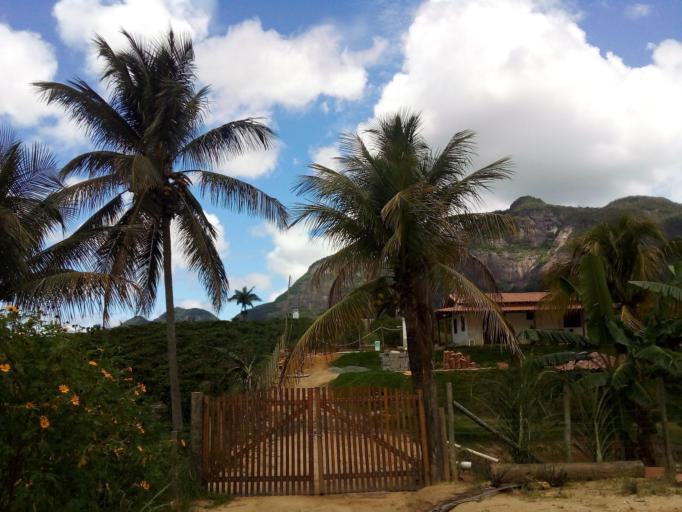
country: BR
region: Espirito Santo
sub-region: Ibiracu
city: Ibiracu
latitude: -19.8882
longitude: -40.3642
